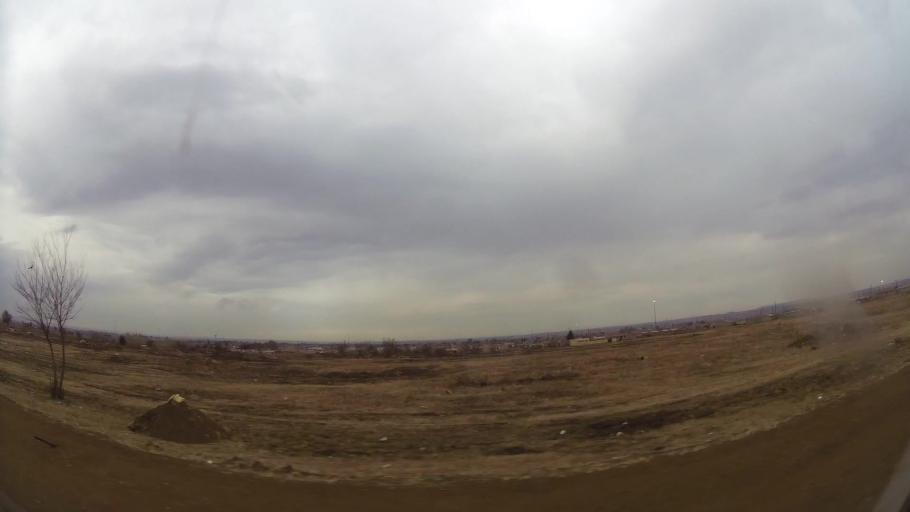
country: ZA
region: Gauteng
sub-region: Ekurhuleni Metropolitan Municipality
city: Germiston
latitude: -26.3851
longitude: 28.1473
